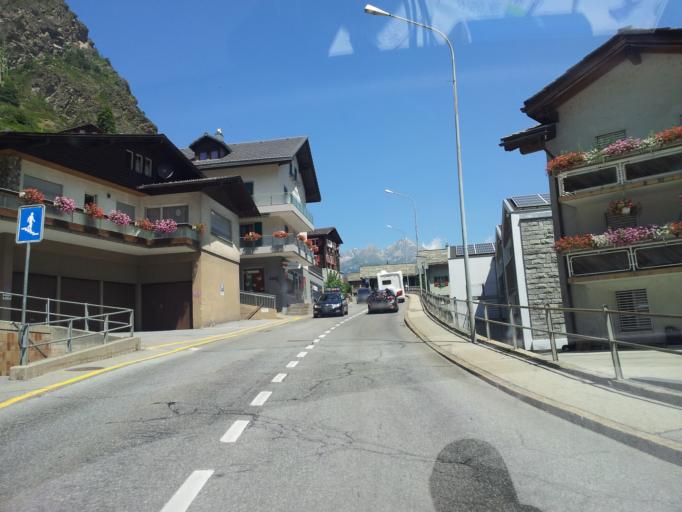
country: CH
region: Valais
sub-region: Visp District
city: Stalden
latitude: 46.2327
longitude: 7.8698
